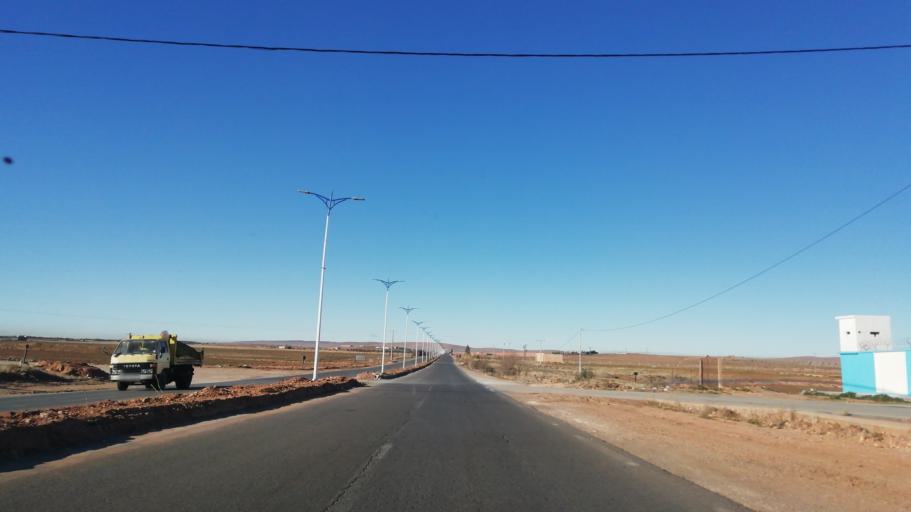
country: DZ
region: El Bayadh
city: El Bayadh
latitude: 33.6908
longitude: 1.0722
